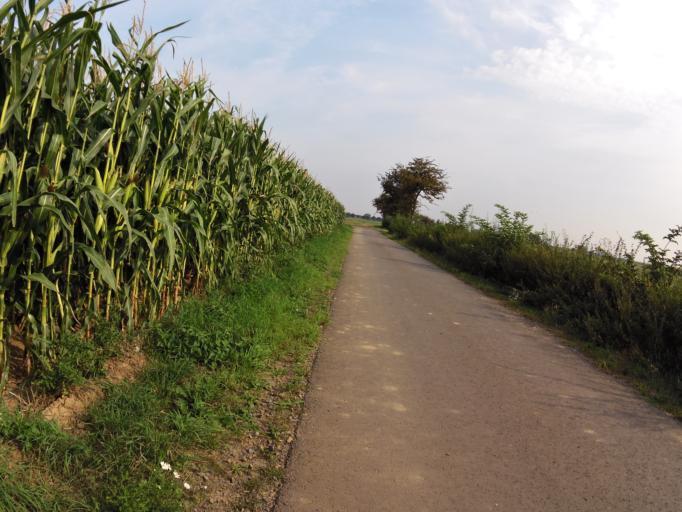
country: DE
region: Lower Saxony
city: Raddestorf
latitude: 52.4680
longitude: 9.0167
